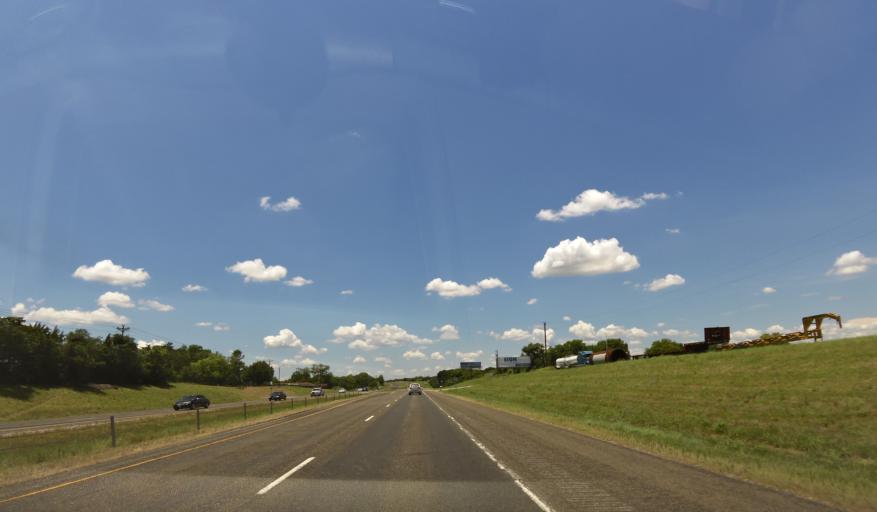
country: US
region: Texas
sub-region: Washington County
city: Brenham
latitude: 30.1908
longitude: -96.5258
